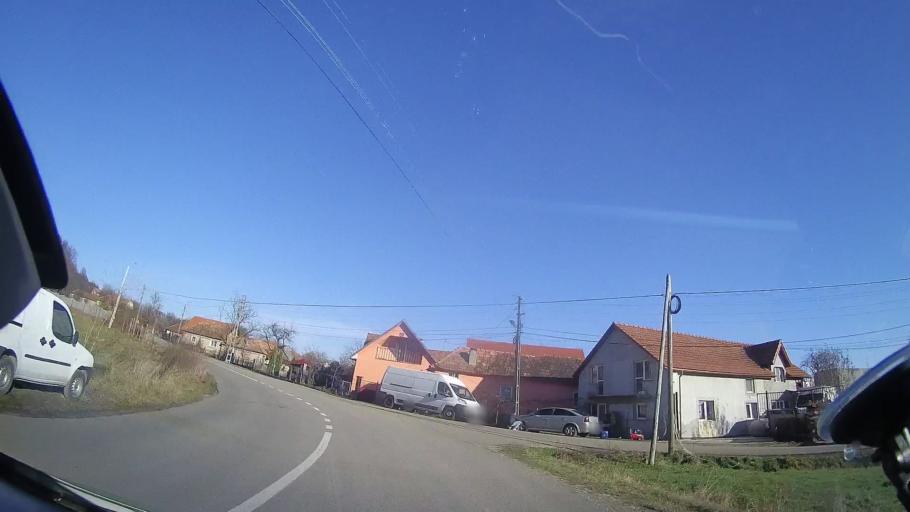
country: RO
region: Bihor
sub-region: Comuna Suncuius
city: Suncuius
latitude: 46.9548
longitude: 22.5361
